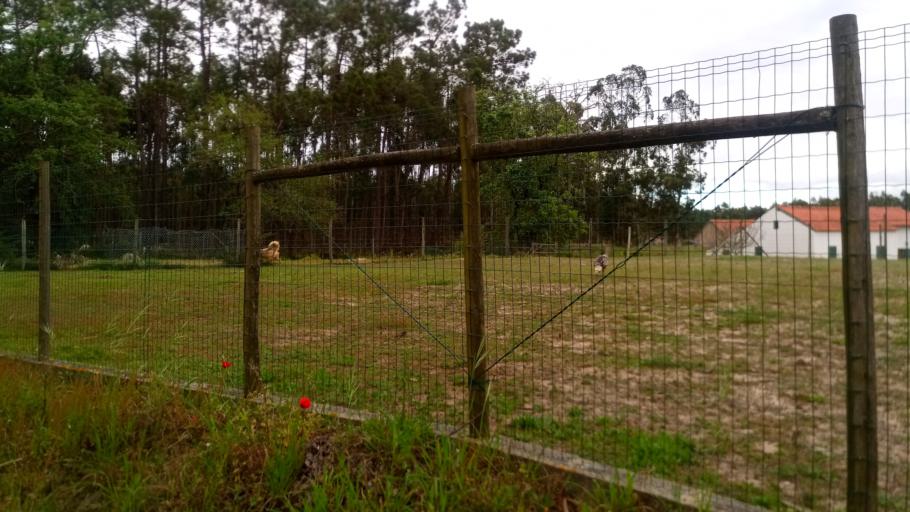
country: PT
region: Leiria
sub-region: Caldas da Rainha
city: Caldas da Rainha
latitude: 39.4562
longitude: -9.1757
